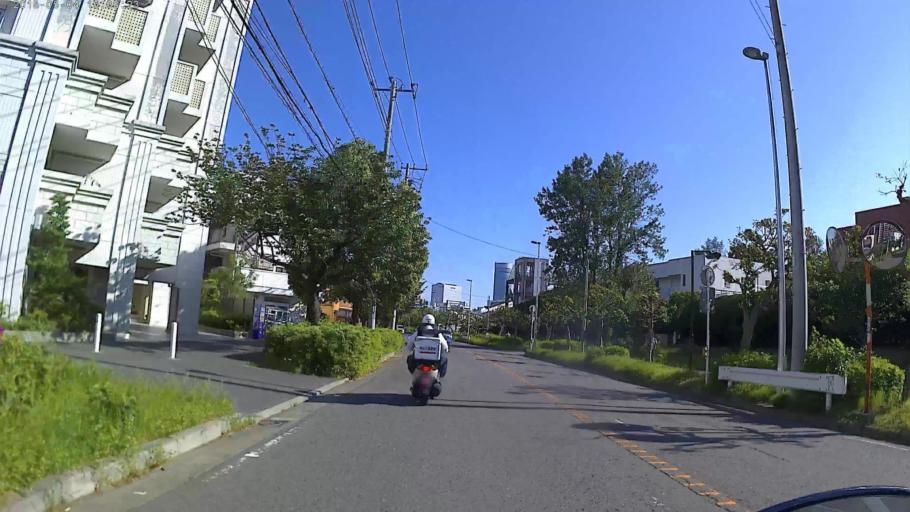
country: JP
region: Kanagawa
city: Yokohama
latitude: 35.5208
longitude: 139.6202
